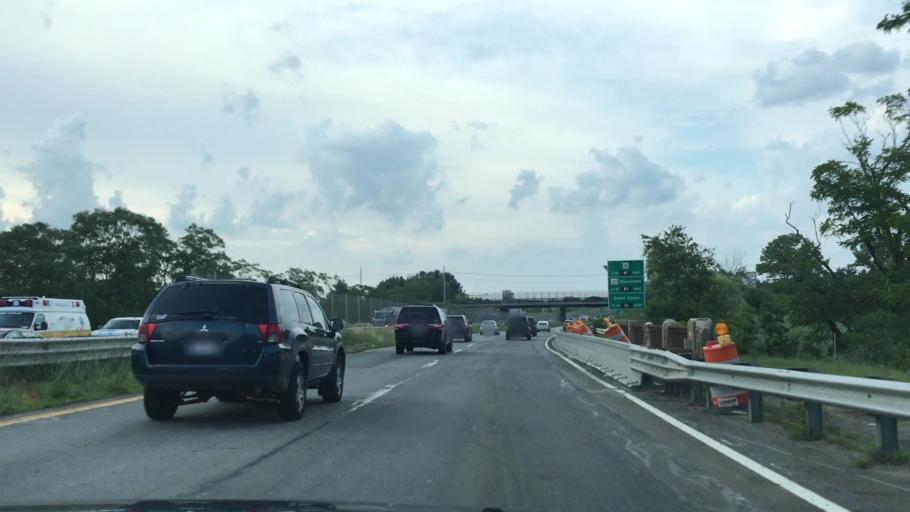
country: US
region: Massachusetts
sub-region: Essex County
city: Peabody
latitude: 42.5469
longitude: -70.9365
